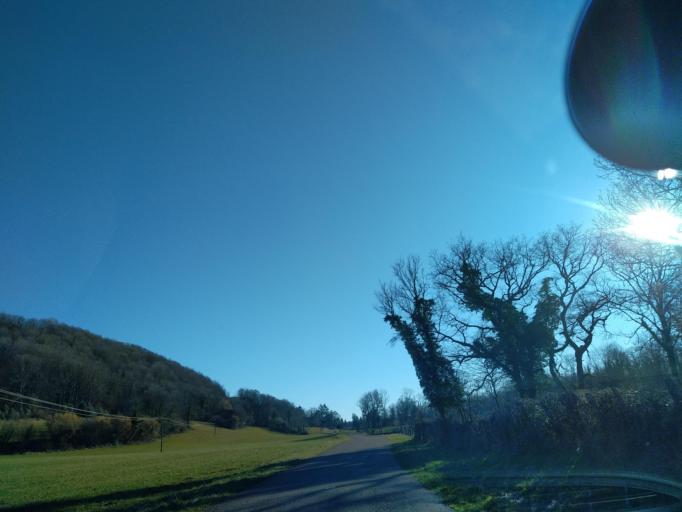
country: FR
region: Franche-Comte
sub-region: Departement du Jura
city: Clairvaux-les-Lacs
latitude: 46.7064
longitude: 5.7349
